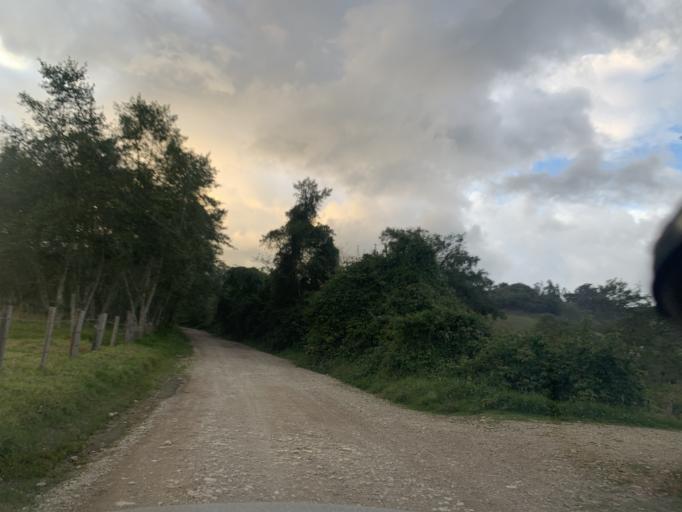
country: CO
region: Boyaca
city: La Capilla
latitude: 5.7326
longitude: -73.4955
